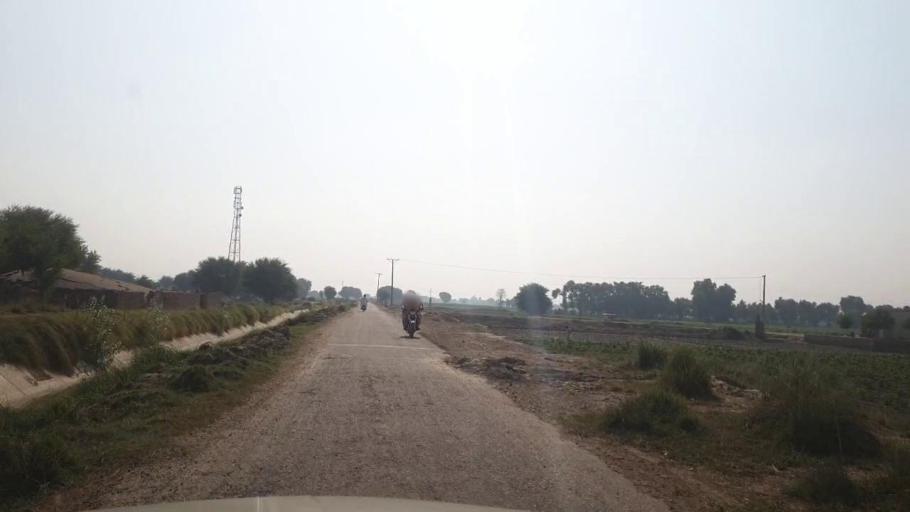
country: PK
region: Sindh
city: Bhan
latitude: 26.5300
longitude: 67.7779
